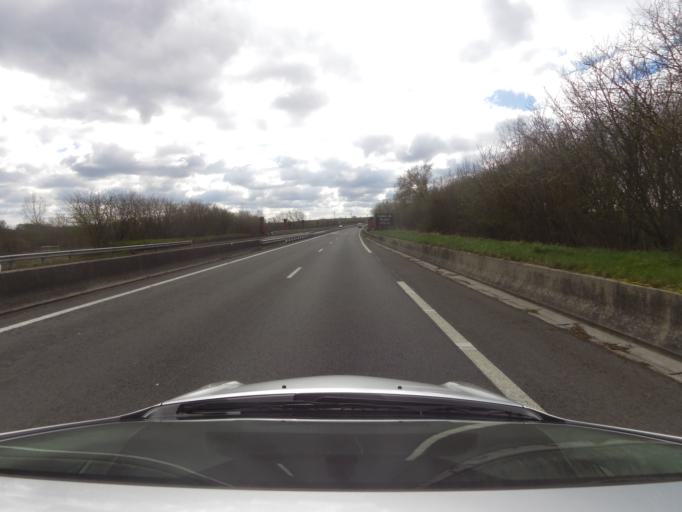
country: FR
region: Picardie
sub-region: Departement de la Somme
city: Rue
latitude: 50.3252
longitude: 1.7160
